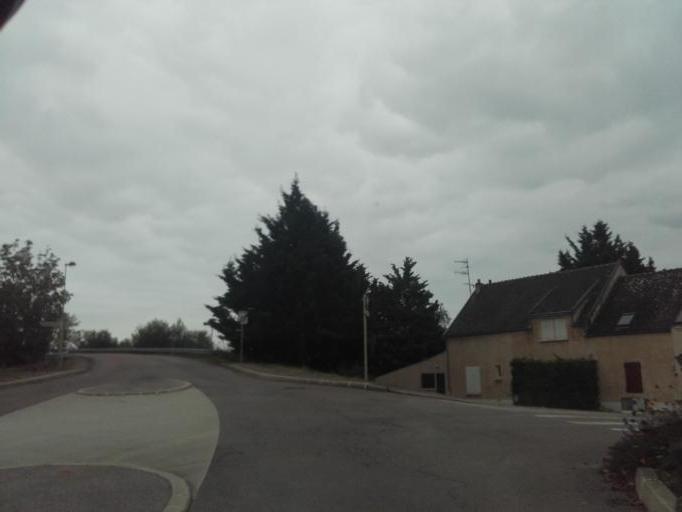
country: FR
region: Bourgogne
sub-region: Departement de la Cote-d'Or
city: Bligny-les-Beaune
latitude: 46.9900
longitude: 4.8510
